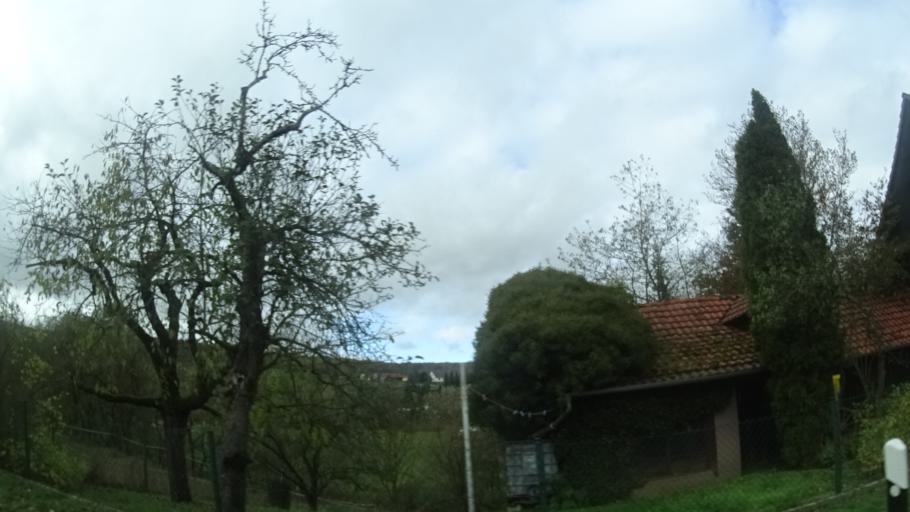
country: DE
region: Bavaria
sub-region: Regierungsbezirk Unterfranken
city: Aubstadt
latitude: 50.3557
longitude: 10.4229
